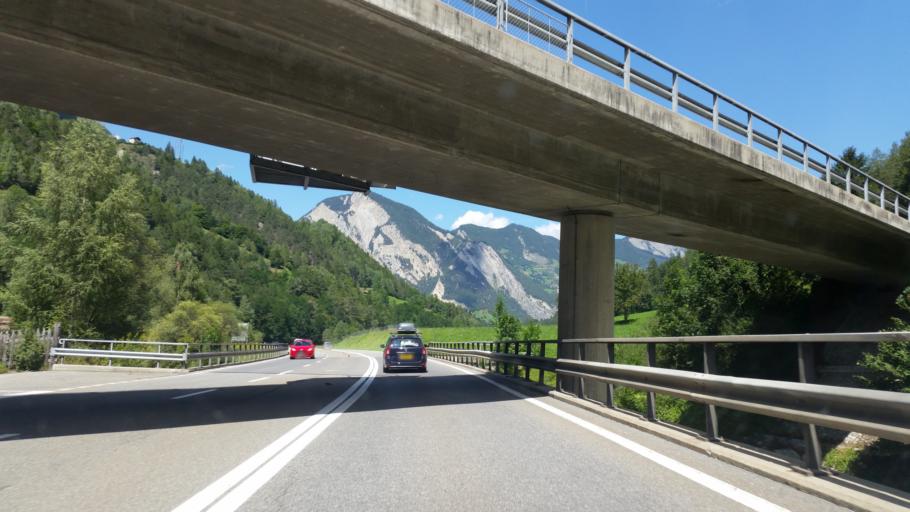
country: CH
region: Valais
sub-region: Entremont District
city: Orsieres
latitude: 46.0446
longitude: 7.1489
